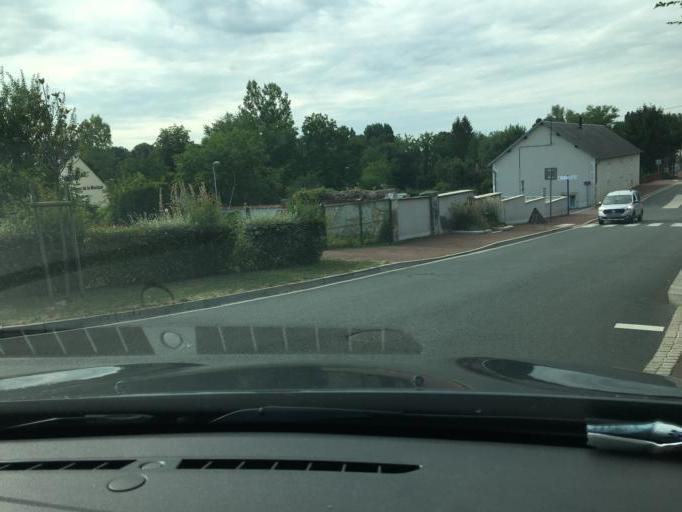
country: FR
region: Centre
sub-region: Departement du Cher
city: Rians
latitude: 47.2005
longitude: 2.5714
